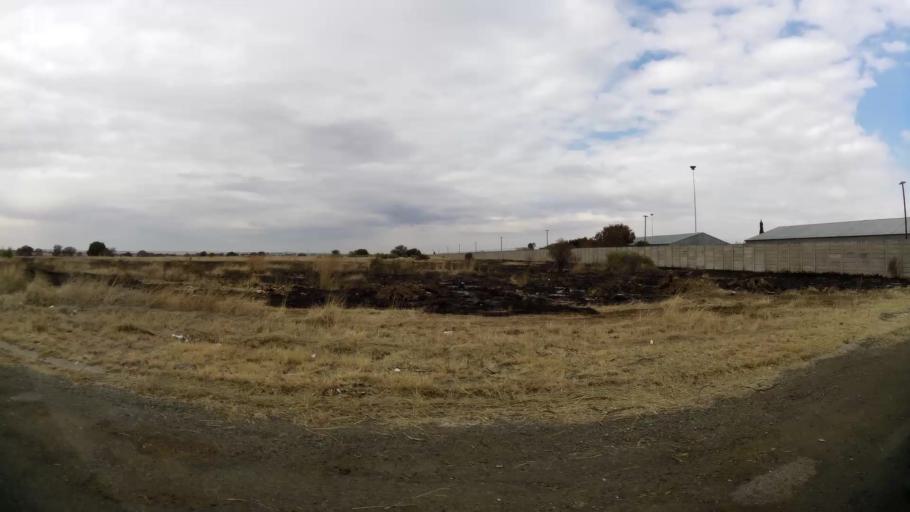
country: ZA
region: Orange Free State
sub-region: Fezile Dabi District Municipality
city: Kroonstad
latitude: -27.6358
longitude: 27.2427
